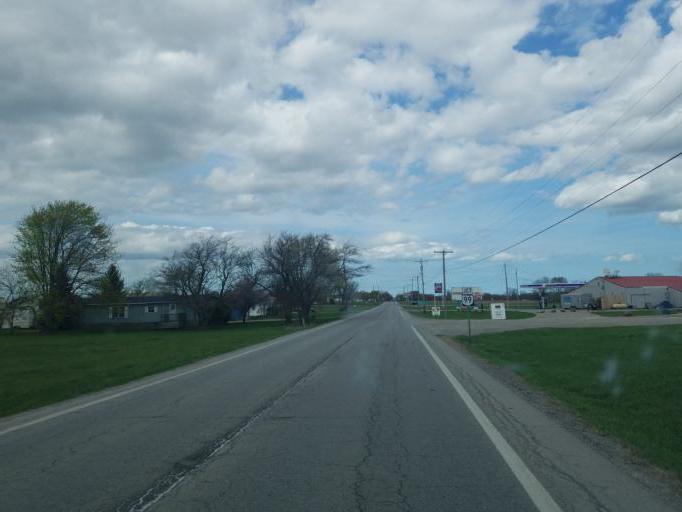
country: US
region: Ohio
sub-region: Erie County
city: Sandusky
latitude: 41.3502
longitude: -82.7546
